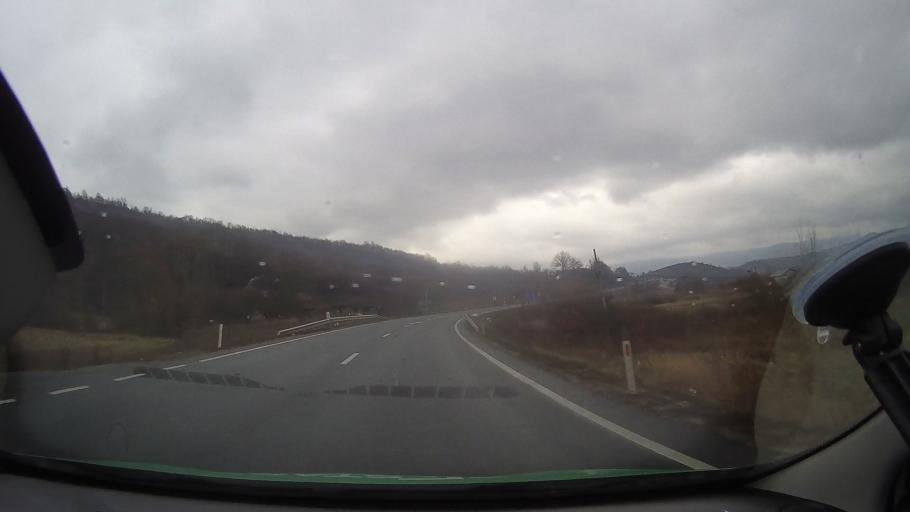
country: RO
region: Hunedoara
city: Vata de Jos
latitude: 46.2132
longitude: 22.5789
